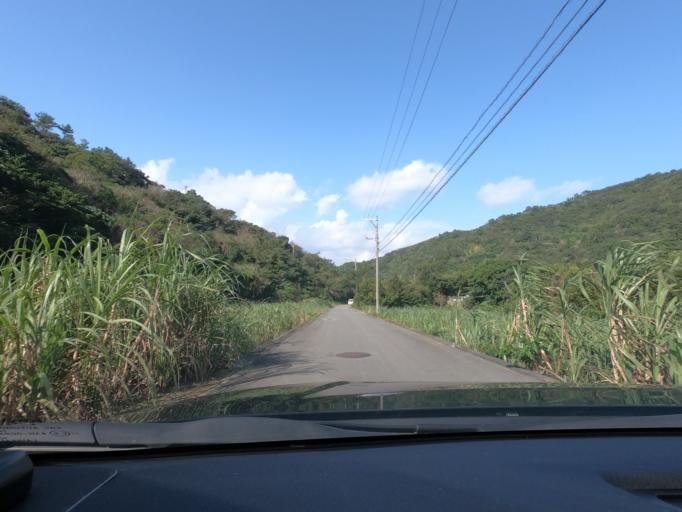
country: JP
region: Okinawa
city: Nago
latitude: 26.7650
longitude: 128.2117
